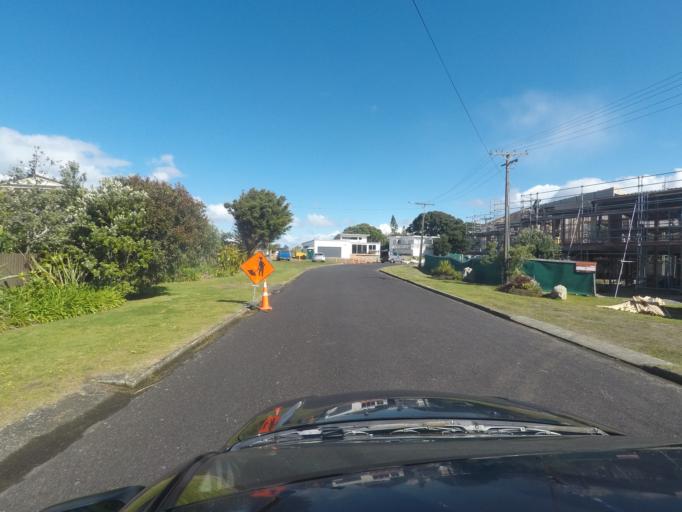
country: NZ
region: Bay of Plenty
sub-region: Western Bay of Plenty District
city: Waihi Beach
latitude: -37.4184
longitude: 175.9509
